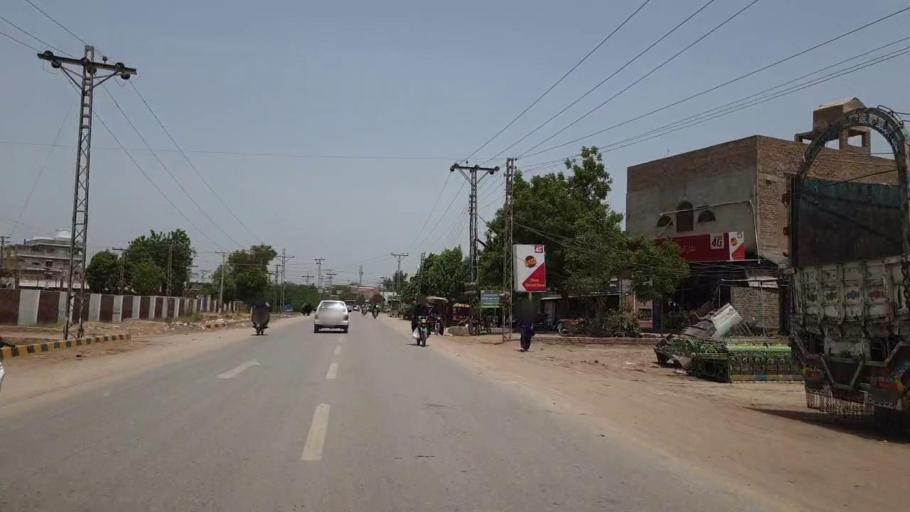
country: PK
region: Sindh
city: Nawabshah
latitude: 26.2504
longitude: 68.4271
